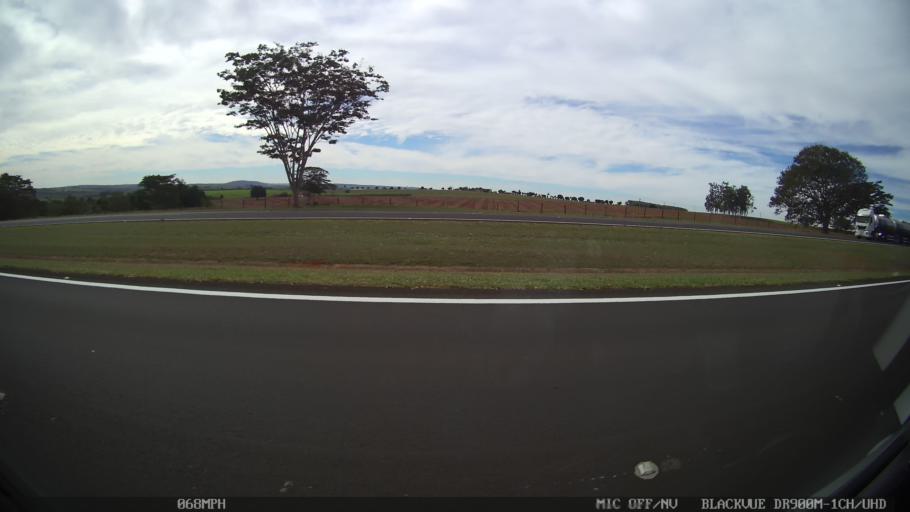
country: BR
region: Sao Paulo
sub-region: Taquaritinga
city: Taquaritinga
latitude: -21.4669
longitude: -48.6114
